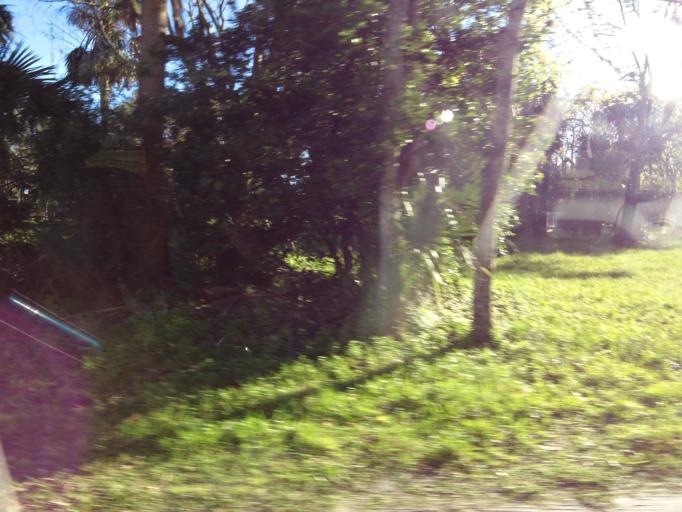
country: US
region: Florida
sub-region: Duval County
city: Atlantic Beach
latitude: 30.3917
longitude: -81.4290
